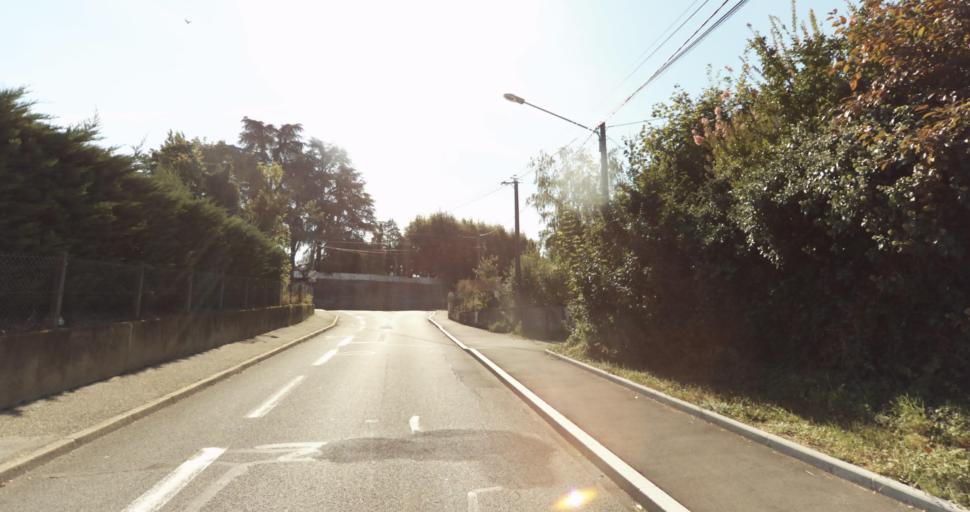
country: FR
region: Rhone-Alpes
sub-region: Departement du Rhone
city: Neuville-sur-Saone
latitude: 45.8720
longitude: 4.8465
